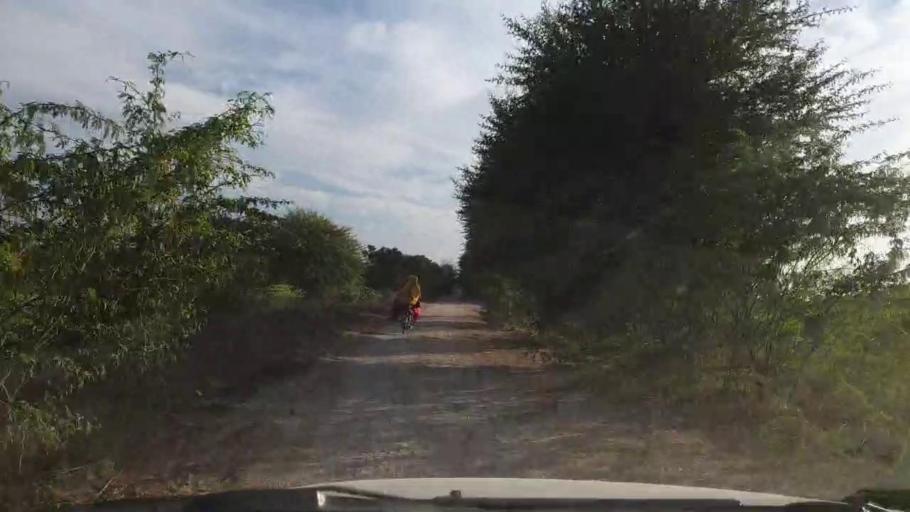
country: PK
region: Sindh
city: Pithoro
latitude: 25.6427
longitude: 69.2919
